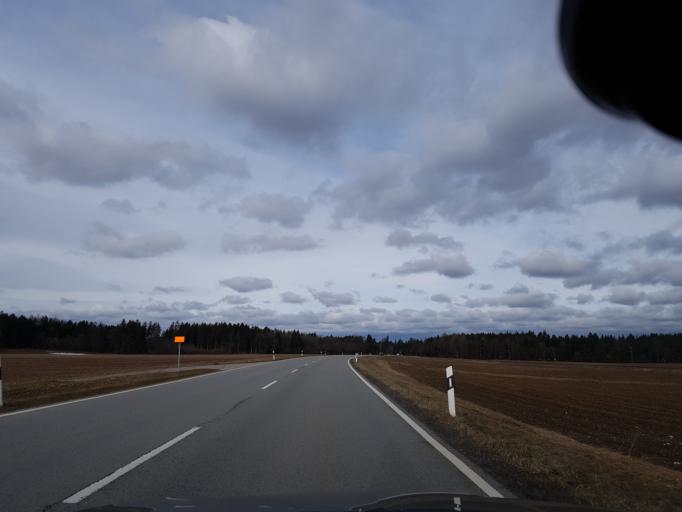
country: DE
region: Bavaria
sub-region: Upper Bavaria
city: Aying
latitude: 47.9752
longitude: 11.7595
